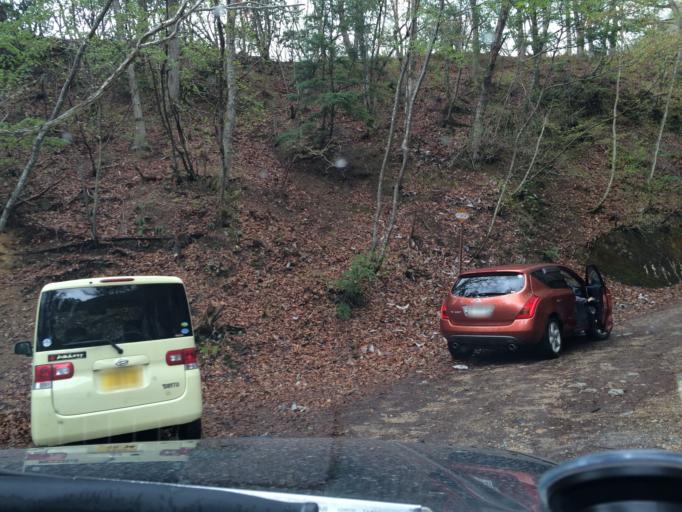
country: JP
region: Nagano
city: Omachi
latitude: 36.5076
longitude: 137.7986
